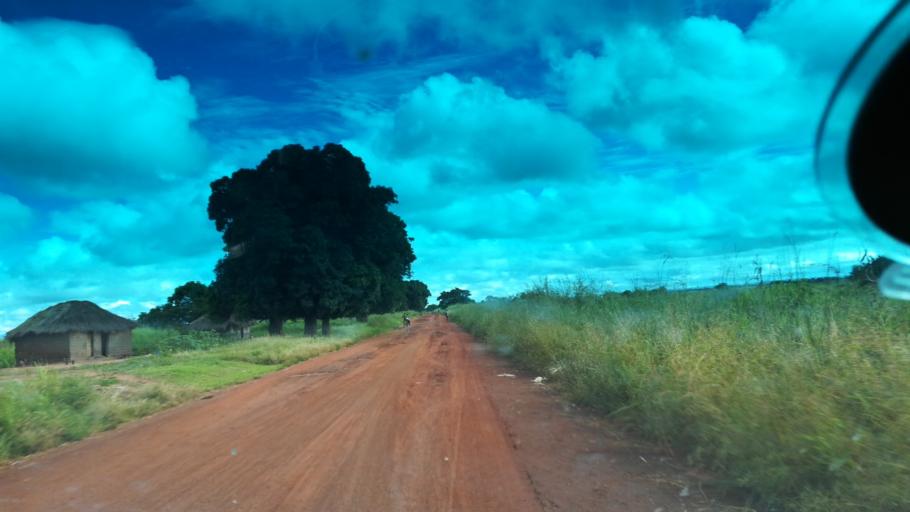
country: ZM
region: Luapula
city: Nchelenge
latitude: -9.2688
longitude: 28.3122
